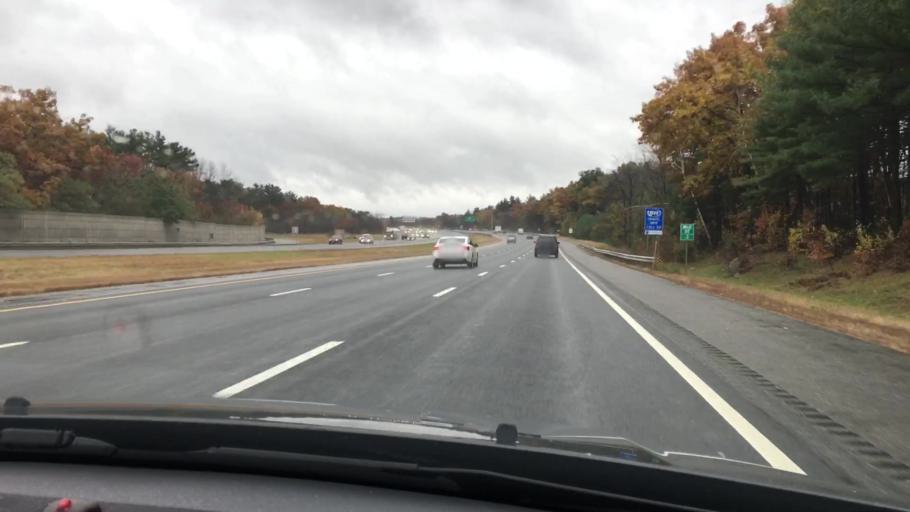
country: US
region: Massachusetts
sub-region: Middlesex County
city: Tyngsboro
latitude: 42.6357
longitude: -71.4095
